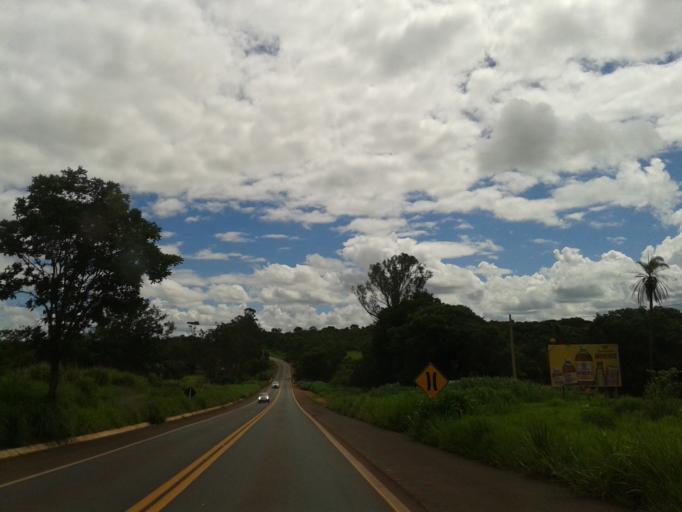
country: BR
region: Minas Gerais
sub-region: Ituiutaba
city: Ituiutaba
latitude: -18.9188
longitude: -49.4172
